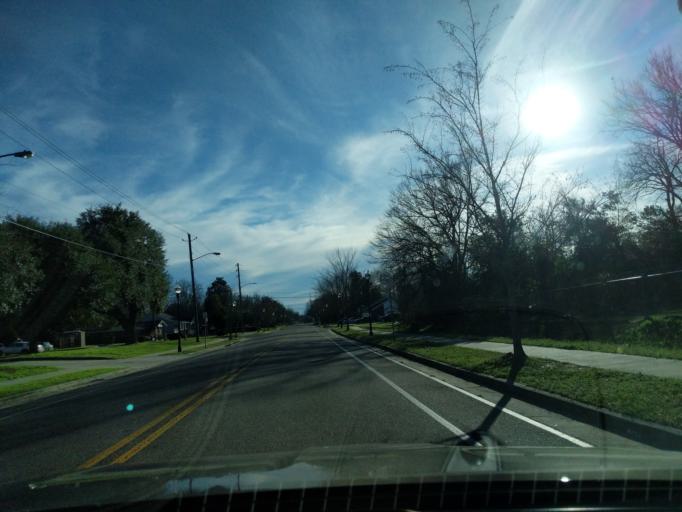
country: US
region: Georgia
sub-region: Richmond County
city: Augusta
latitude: 33.4613
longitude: -81.9519
